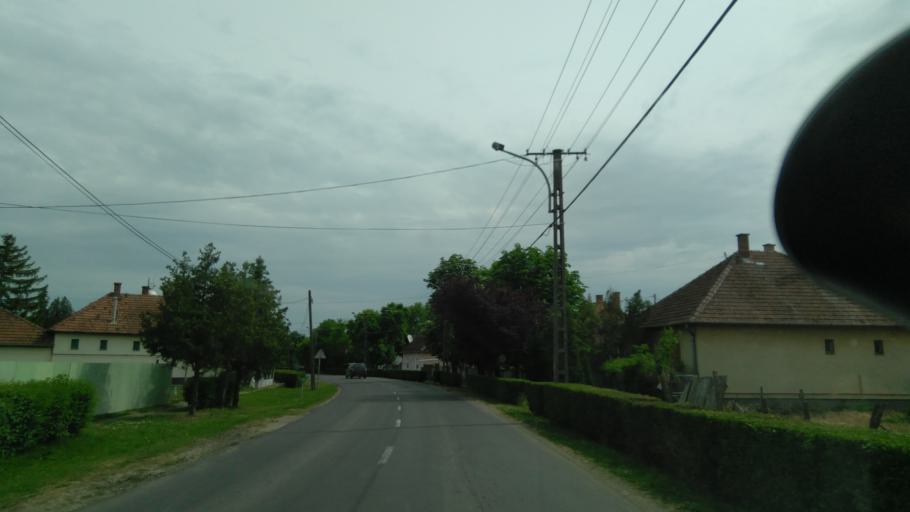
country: HU
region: Bekes
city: Sarkad
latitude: 46.8073
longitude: 21.3807
